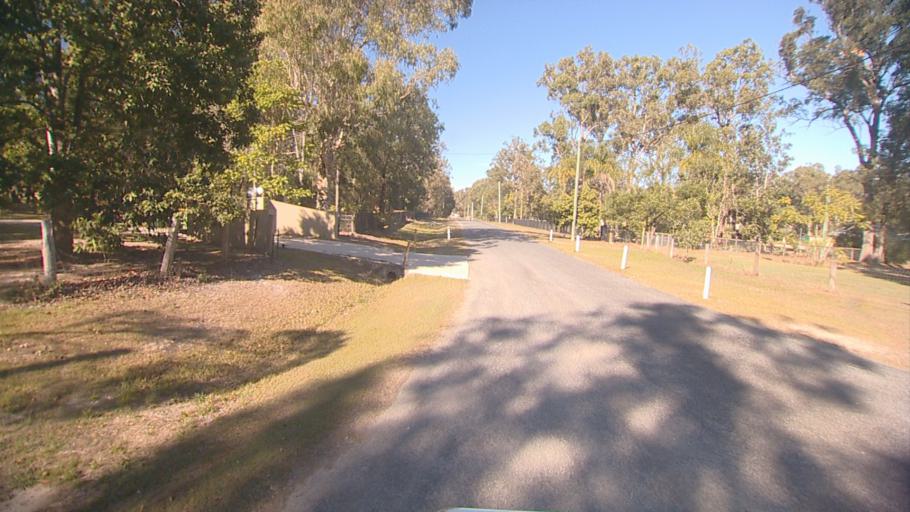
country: AU
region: Queensland
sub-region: Logan
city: Chambers Flat
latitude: -27.7843
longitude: 153.1257
